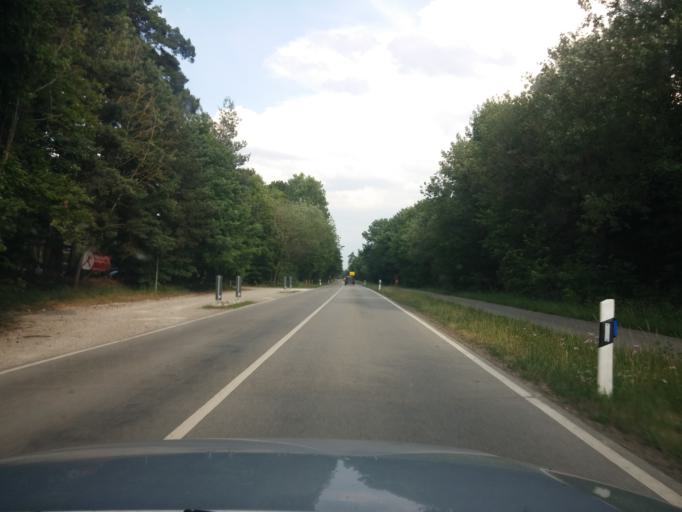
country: DE
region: Bavaria
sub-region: Upper Bavaria
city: Vaterstetten
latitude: 48.1183
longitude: 11.7618
